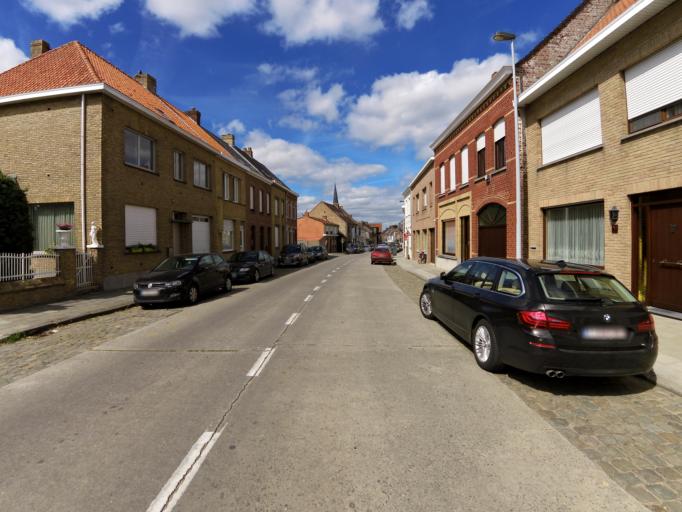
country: FR
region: Nord-Pas-de-Calais
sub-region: Departement du Nord
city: Steenvoorde
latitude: 50.8567
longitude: 2.6203
